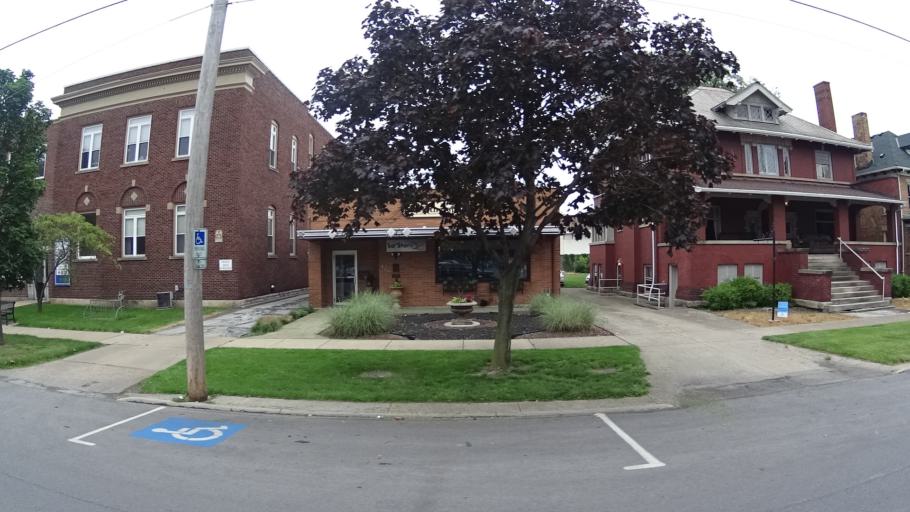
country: US
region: Ohio
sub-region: Erie County
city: Sandusky
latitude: 41.4530
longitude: -82.7099
